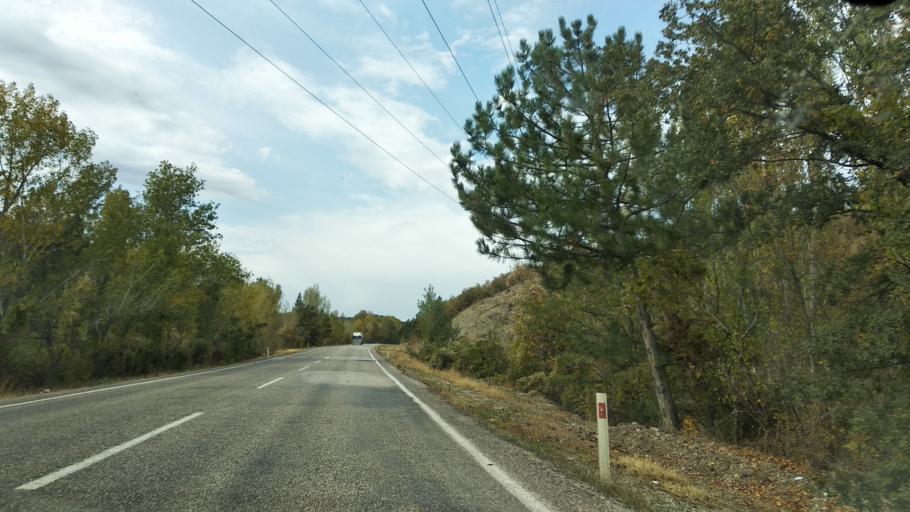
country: TR
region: Ankara
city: Nallihan
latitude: 40.3080
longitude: 31.2815
